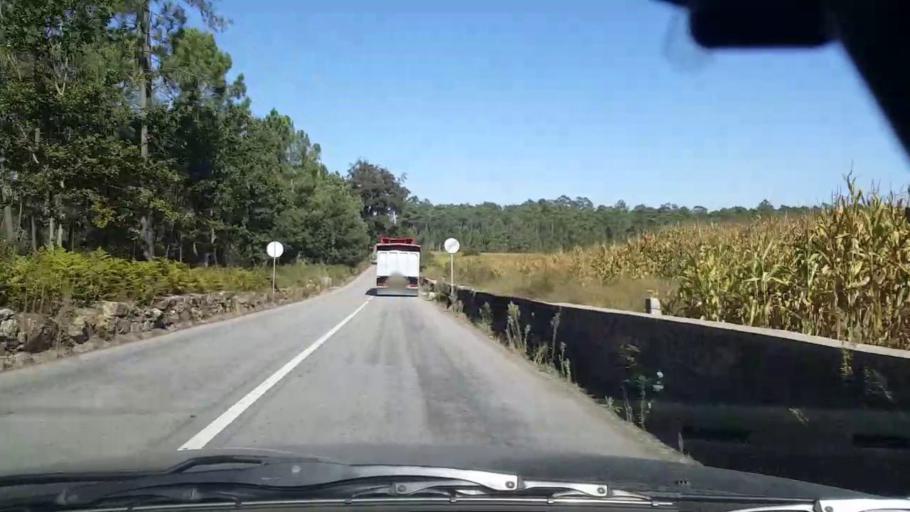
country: PT
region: Braga
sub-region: Vila Nova de Famalicao
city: Ribeirao
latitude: 41.3653
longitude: -8.6215
